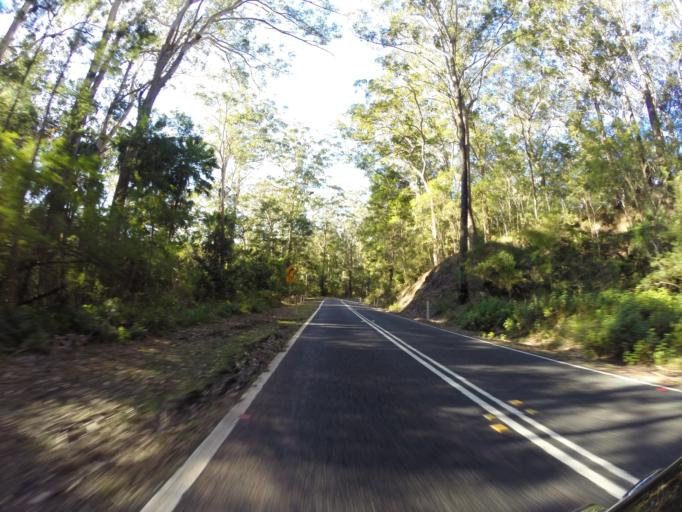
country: AU
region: New South Wales
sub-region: Wollongong
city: Helensburgh
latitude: -34.1527
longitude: 151.0208
